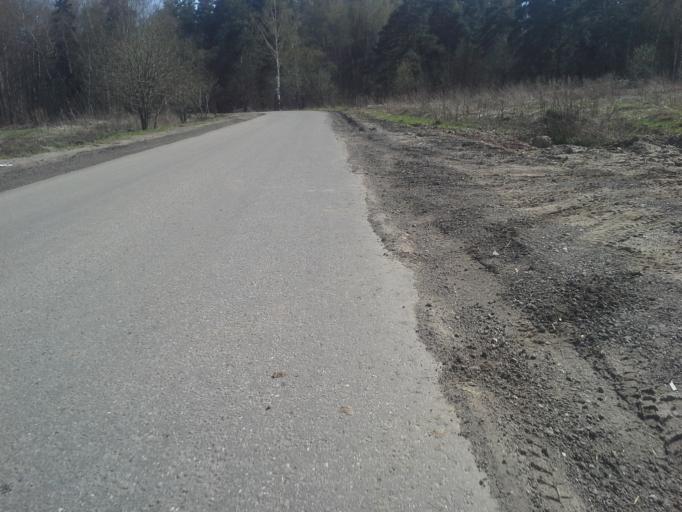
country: RU
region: Moskovskaya
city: Dubrovitsy
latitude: 55.4658
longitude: 37.4407
